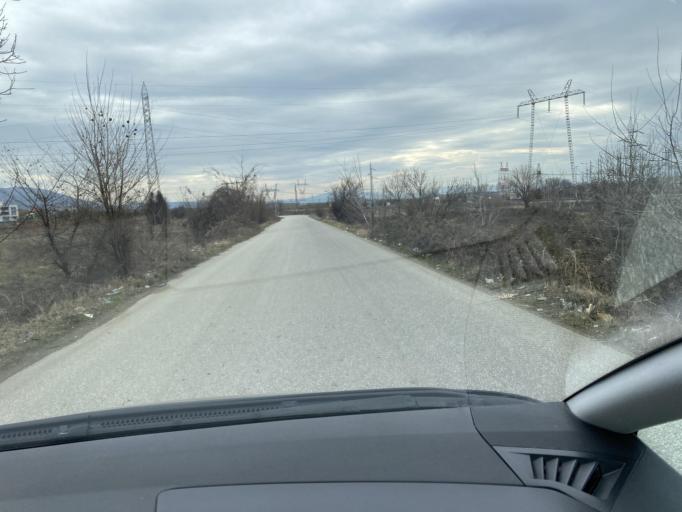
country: MK
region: Butel
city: Butel
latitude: 42.0420
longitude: 21.4556
